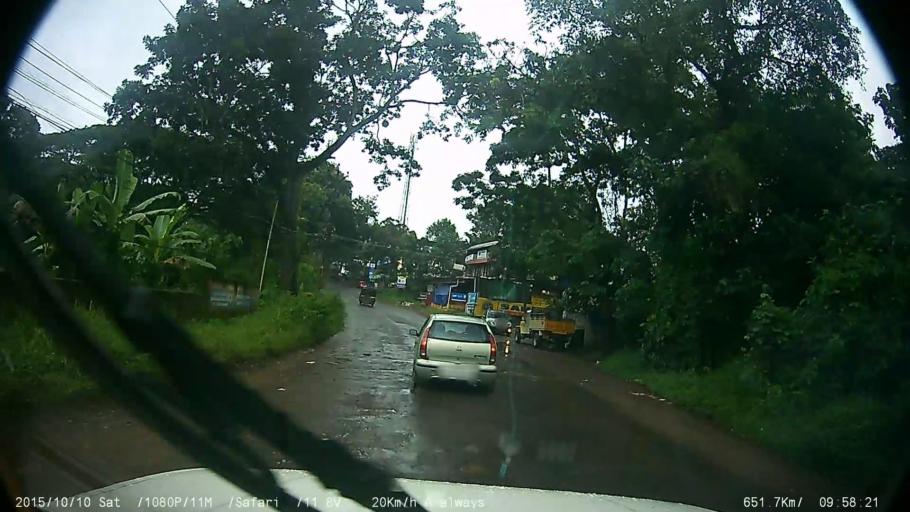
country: IN
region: Kerala
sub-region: Kottayam
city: Kottayam
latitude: 9.6392
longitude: 76.5308
